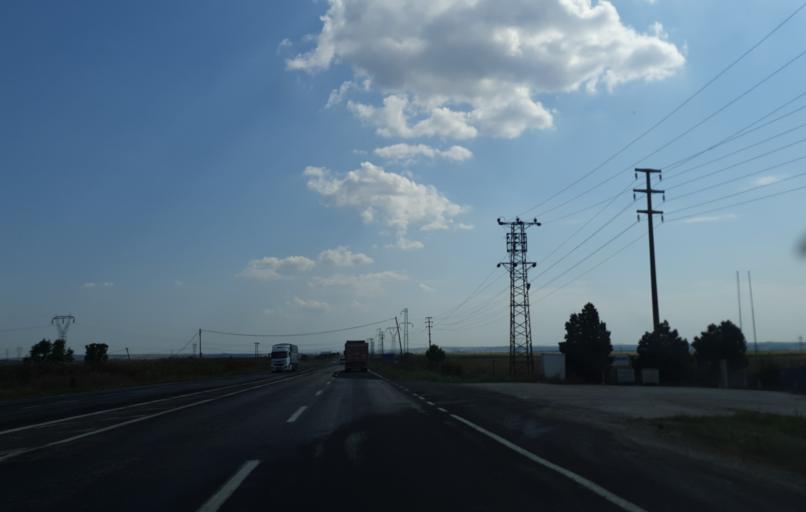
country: TR
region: Kirklareli
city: Buyukkaristiran
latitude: 41.2451
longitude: 27.5395
